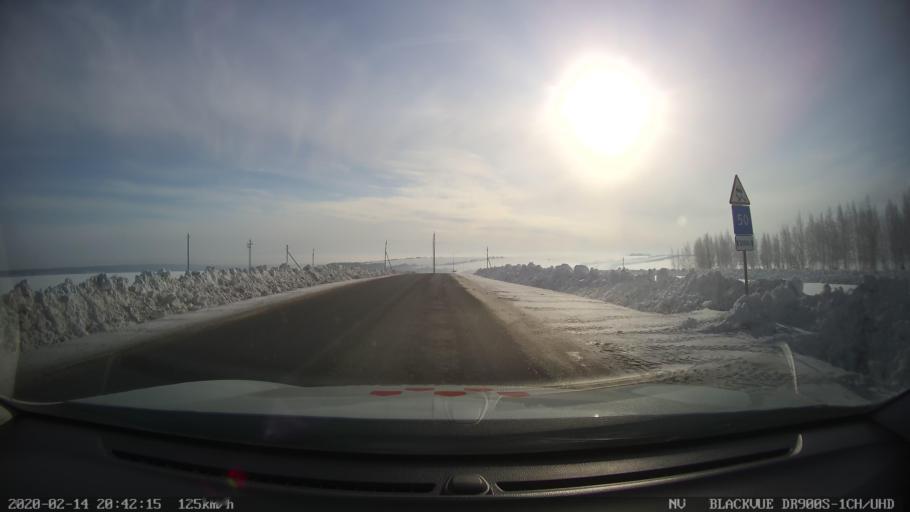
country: RU
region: Tatarstan
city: Kuybyshevskiy Zaton
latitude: 55.3189
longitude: 49.1397
